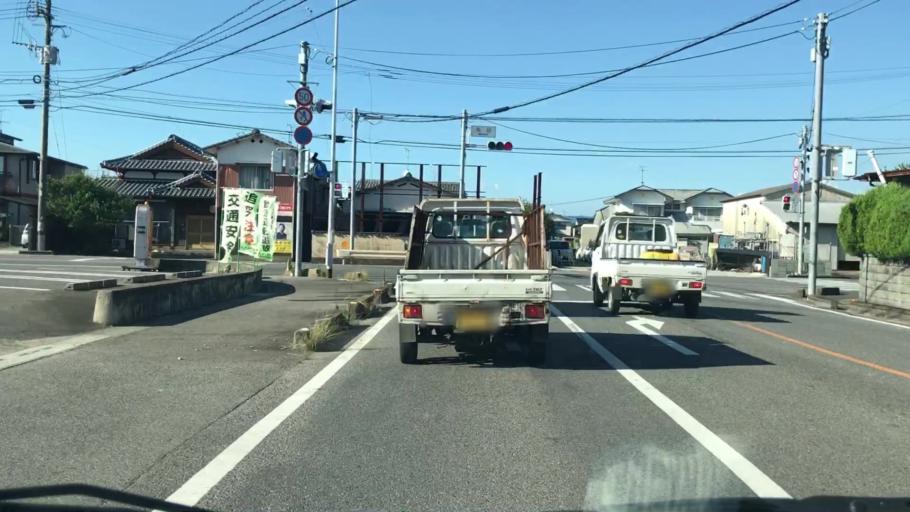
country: JP
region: Saga Prefecture
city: Saga-shi
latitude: 33.2185
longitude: 130.2639
